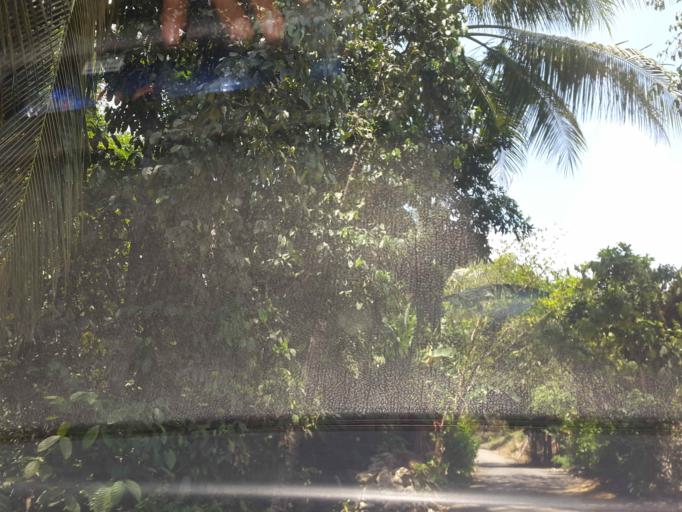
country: ID
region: East Java
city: Sudimoro
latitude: -8.2469
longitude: 111.2173
